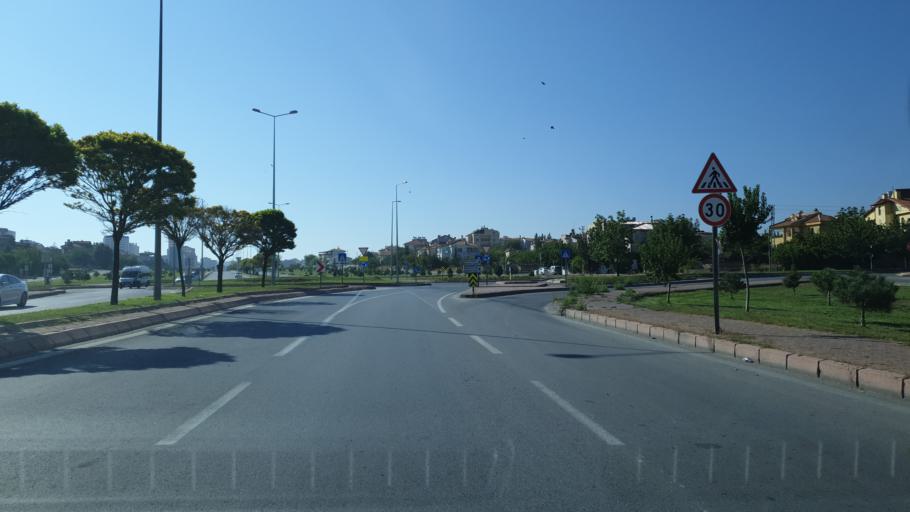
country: TR
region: Kayseri
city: Kocasinan
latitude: 38.7784
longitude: 35.5890
